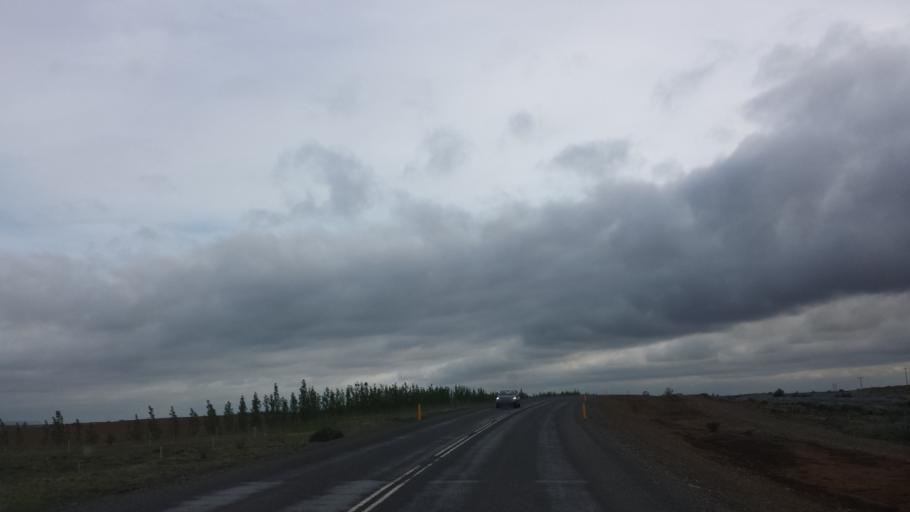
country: IS
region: South
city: Selfoss
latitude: 64.2772
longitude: -20.3492
